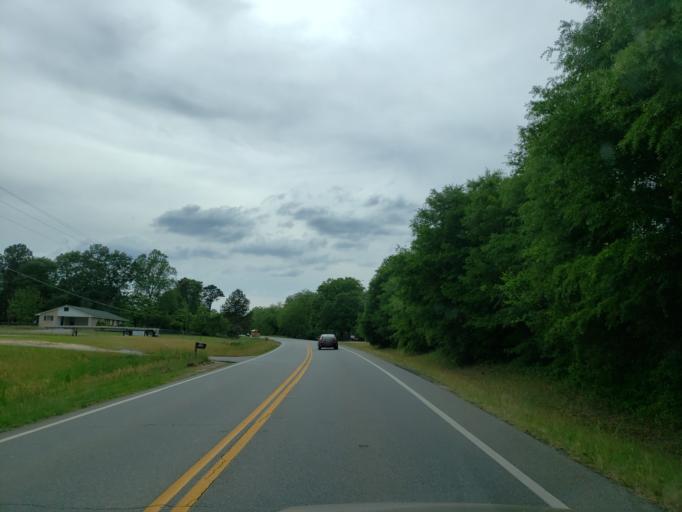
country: US
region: Georgia
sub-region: Houston County
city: Perry
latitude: 32.4469
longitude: -83.7665
